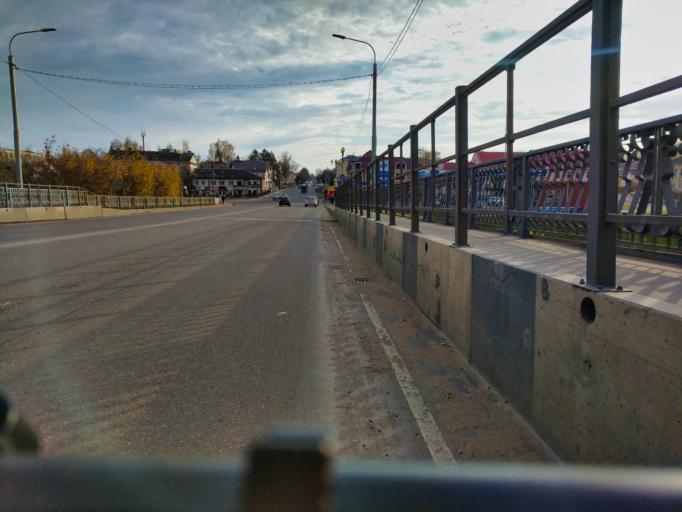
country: RU
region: Tverskaya
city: Rzhev
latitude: 56.2596
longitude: 34.3285
